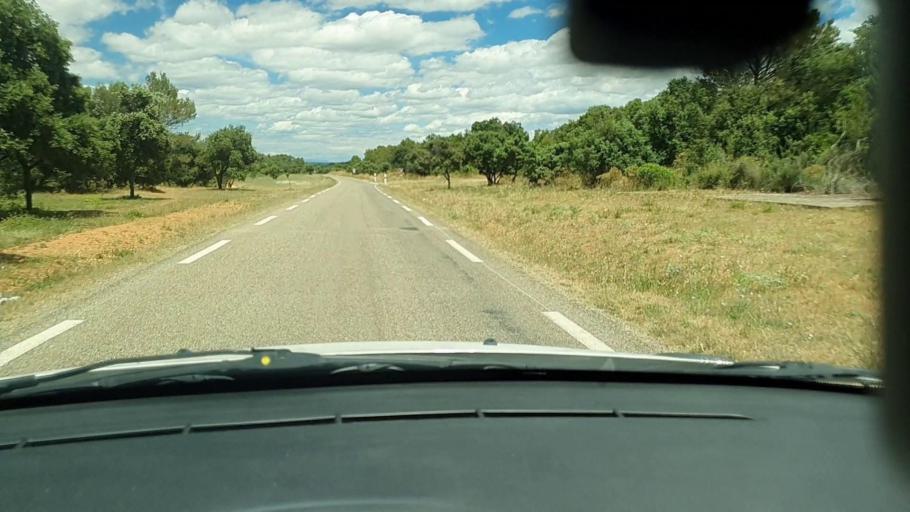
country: FR
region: Languedoc-Roussillon
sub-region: Departement du Gard
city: Cabrieres
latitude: 43.9163
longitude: 4.4741
